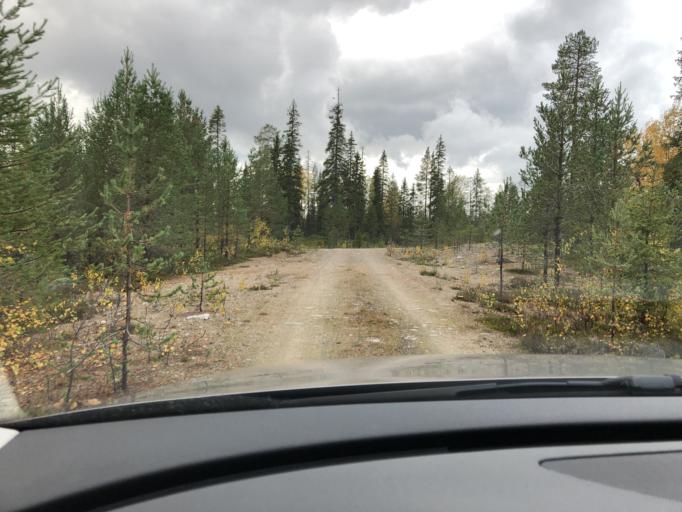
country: FI
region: Northern Ostrobothnia
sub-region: Koillismaa
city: Kuusamo
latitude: 65.9055
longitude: 28.8654
